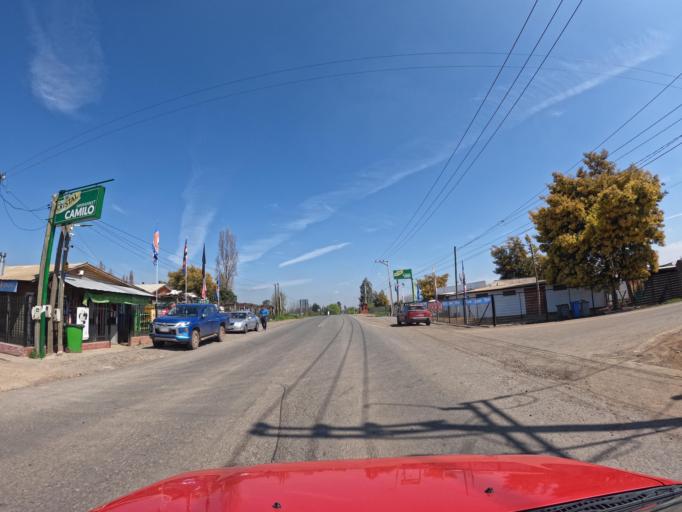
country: CL
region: Maule
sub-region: Provincia de Talca
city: San Clemente
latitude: -35.4910
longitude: -71.3055
